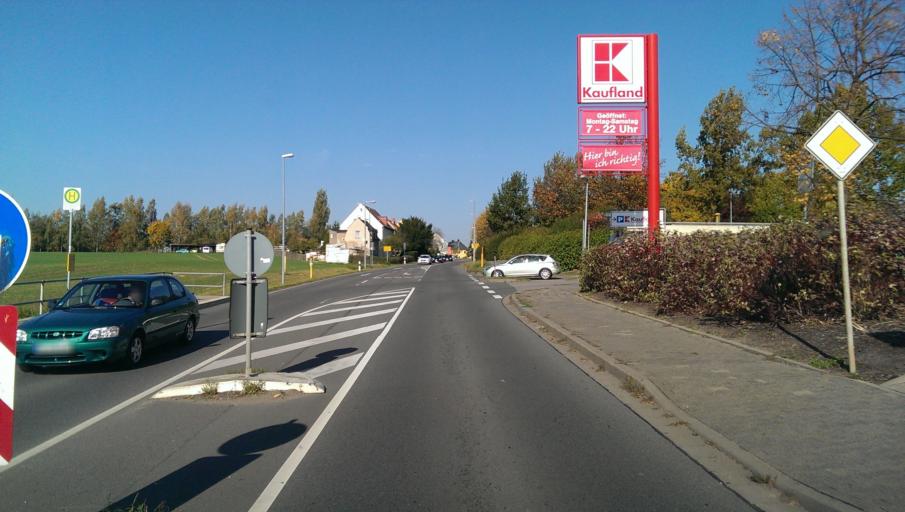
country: DE
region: Saxony
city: Mittweida
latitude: 50.9943
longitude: 12.9641
